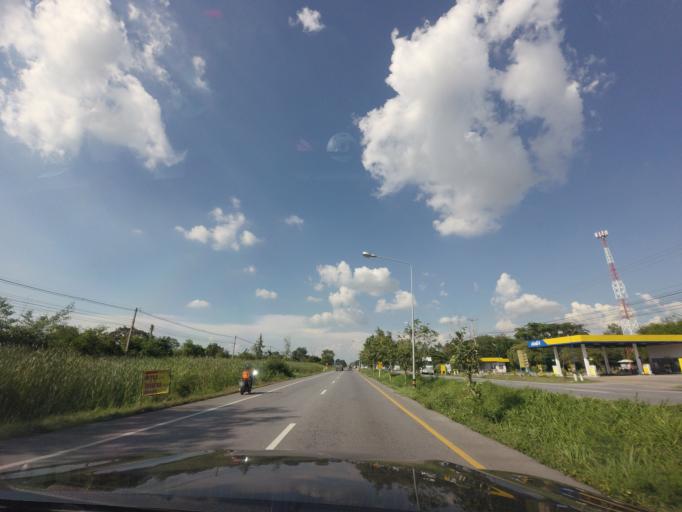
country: TH
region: Khon Kaen
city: Phon
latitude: 15.7307
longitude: 102.5954
